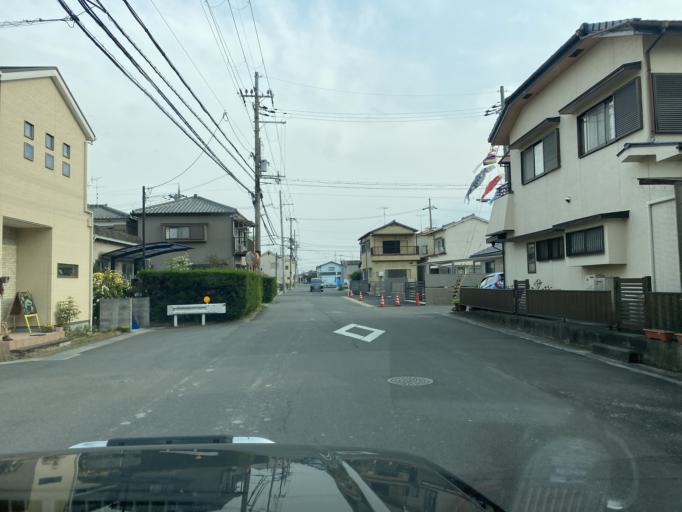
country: JP
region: Kyoto
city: Tanabe
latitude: 34.8136
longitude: 135.7824
